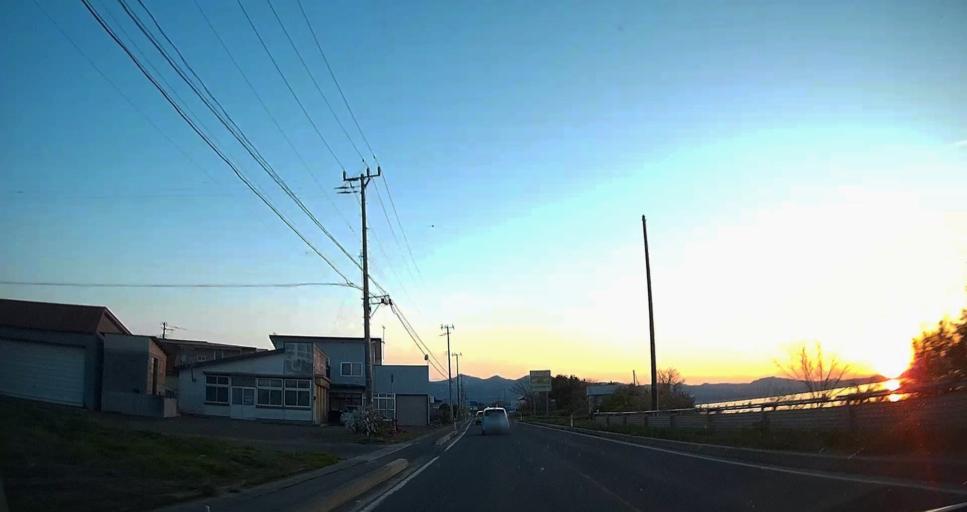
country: JP
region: Aomori
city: Misawa
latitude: 40.8764
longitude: 141.1434
